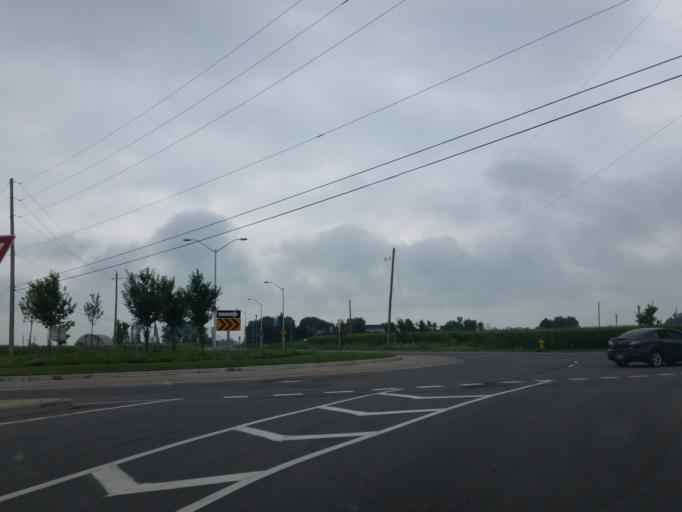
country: CA
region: Ontario
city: Clarence-Rockland
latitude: 45.4578
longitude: -75.4472
